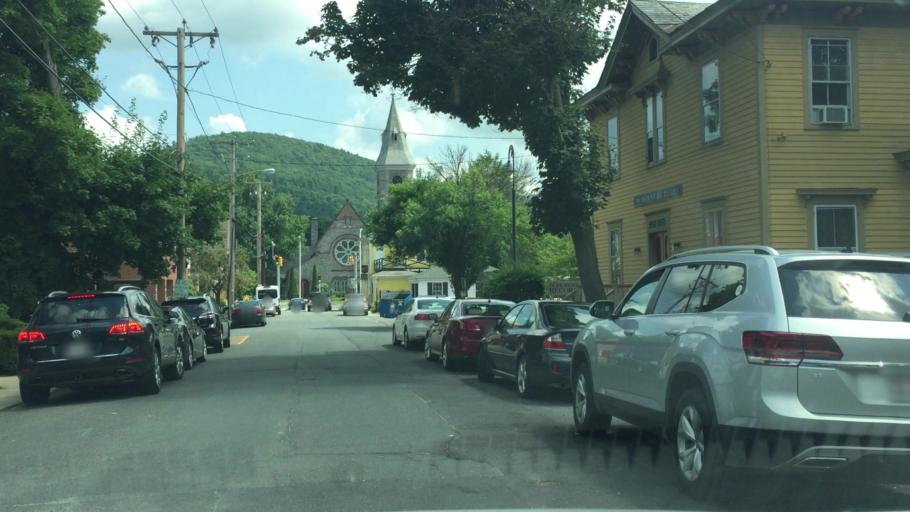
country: US
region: Massachusetts
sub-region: Berkshire County
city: Great Barrington
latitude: 42.1960
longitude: -73.3628
